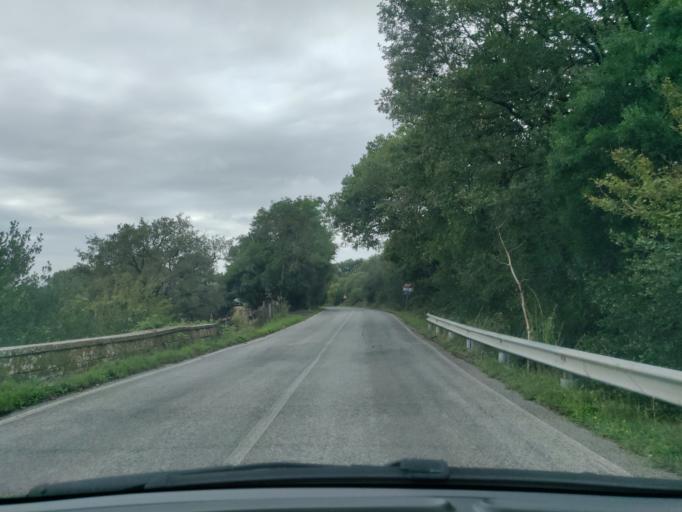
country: IT
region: Latium
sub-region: Citta metropolitana di Roma Capitale
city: Allumiere
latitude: 42.1355
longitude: 11.8705
